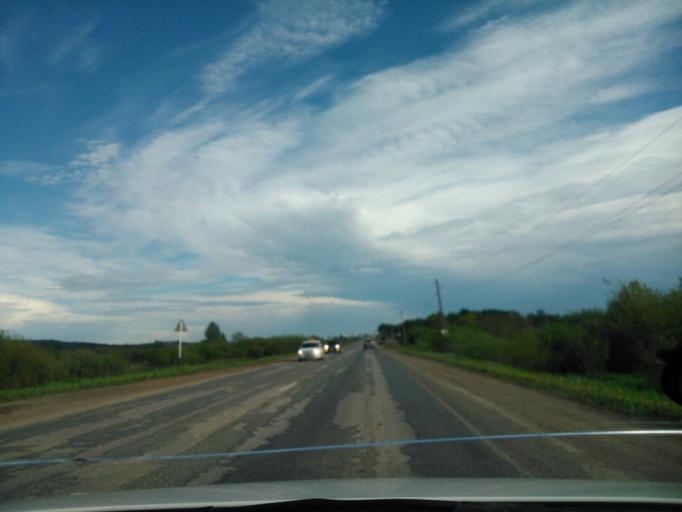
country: RU
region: Perm
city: Lobanovo
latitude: 57.8723
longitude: 56.2808
